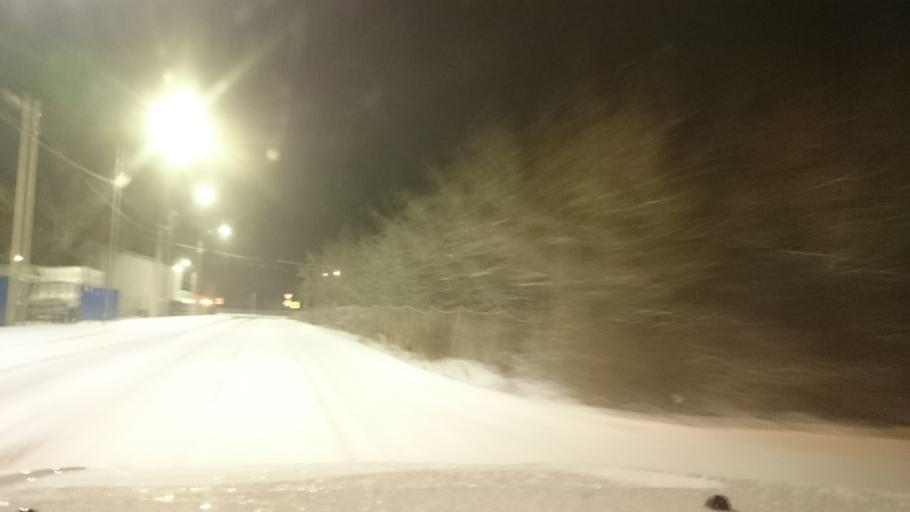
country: RU
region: Tula
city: Kosaya Gora
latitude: 54.1858
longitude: 37.5179
